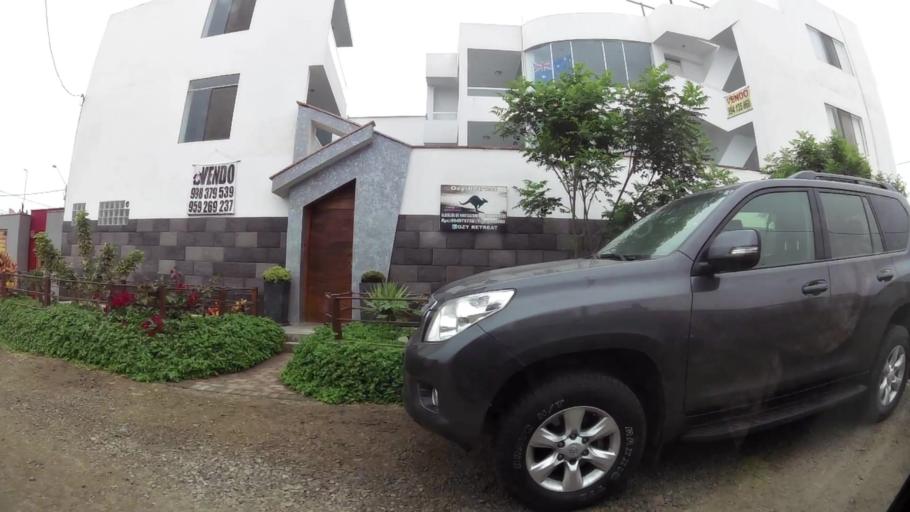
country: PE
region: Lima
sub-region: Lima
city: Punta Hermosa
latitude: -12.3292
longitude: -76.8277
